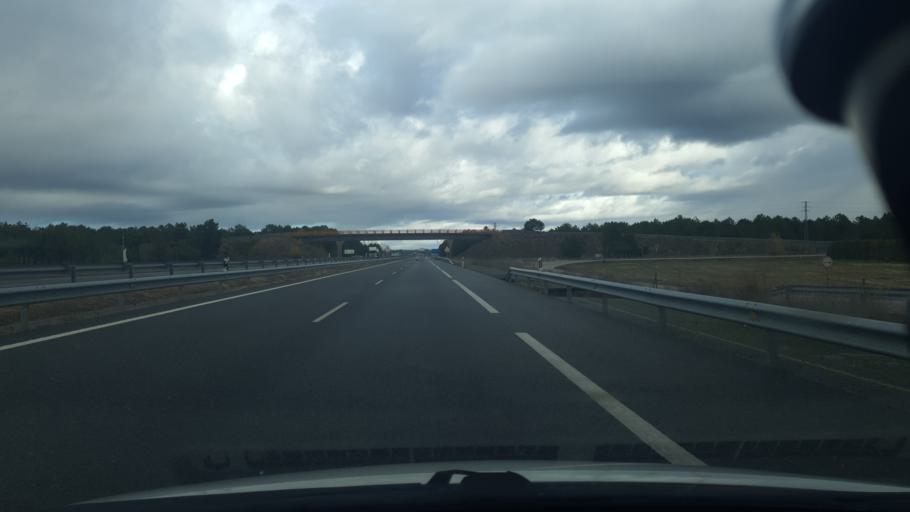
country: ES
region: Castille and Leon
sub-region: Provincia de Segovia
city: Sanchonuno
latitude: 41.3319
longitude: -4.3109
